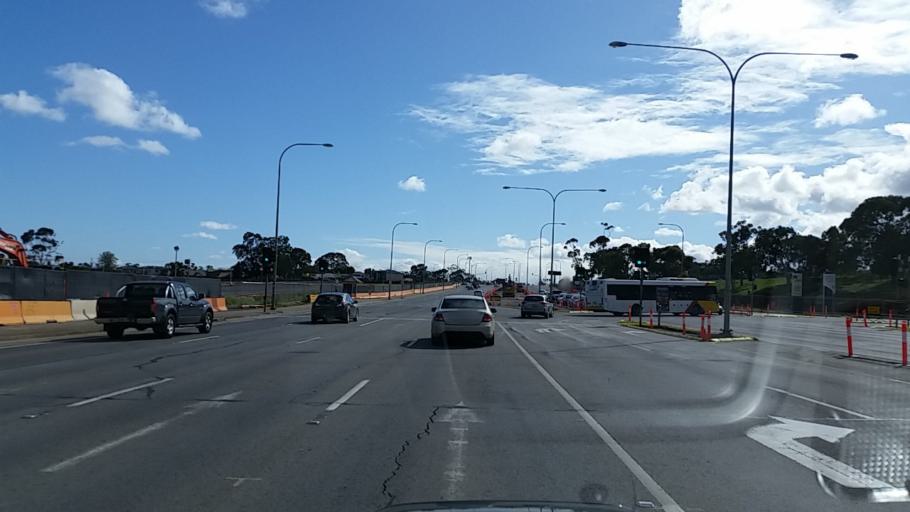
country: AU
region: South Australia
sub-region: Marion
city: Marion
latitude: -35.0197
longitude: 138.5665
